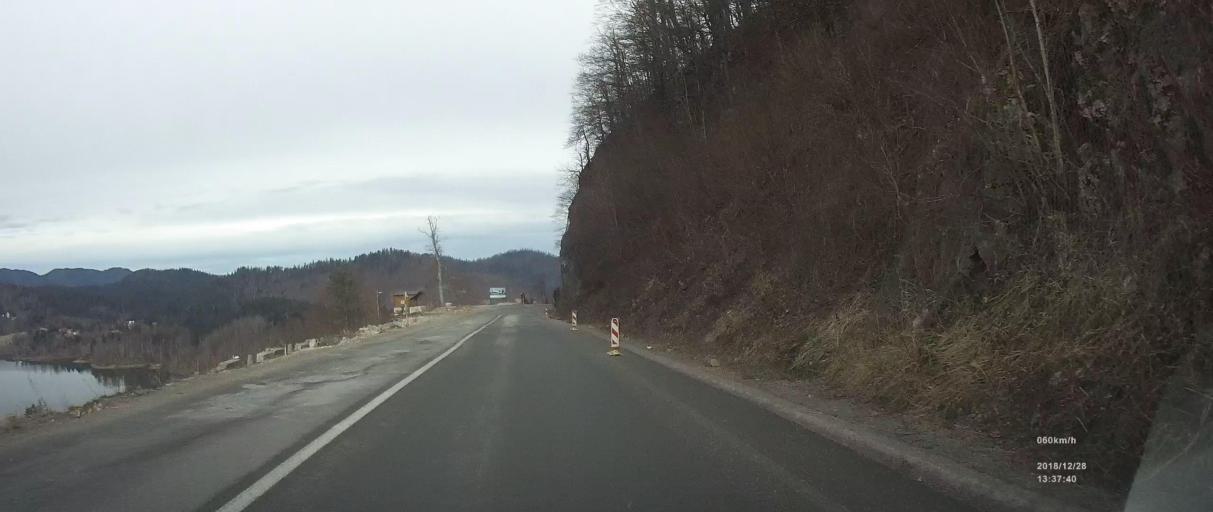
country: HR
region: Primorsko-Goranska
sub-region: Grad Delnice
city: Delnice
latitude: 45.3555
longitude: 14.7168
